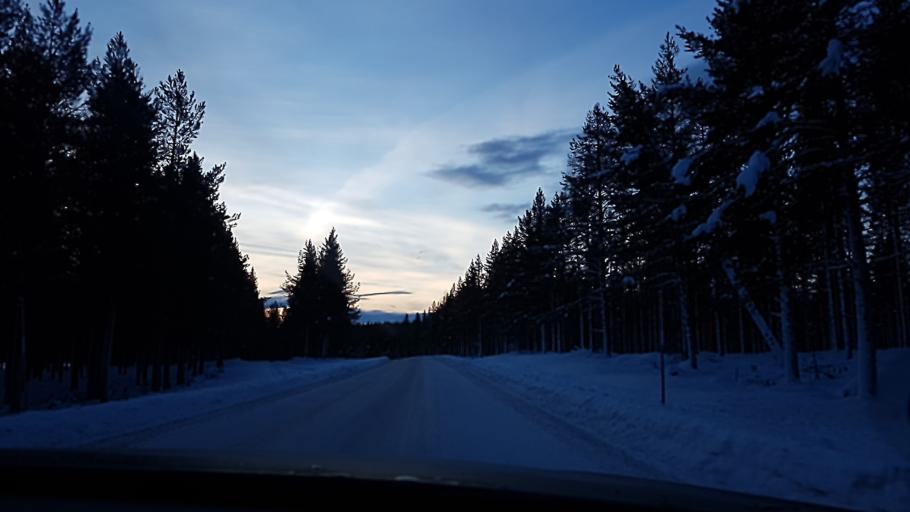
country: SE
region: Norrbotten
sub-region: Arvidsjaurs Kommun
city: Arvidsjaur
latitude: 65.9242
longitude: 19.4569
